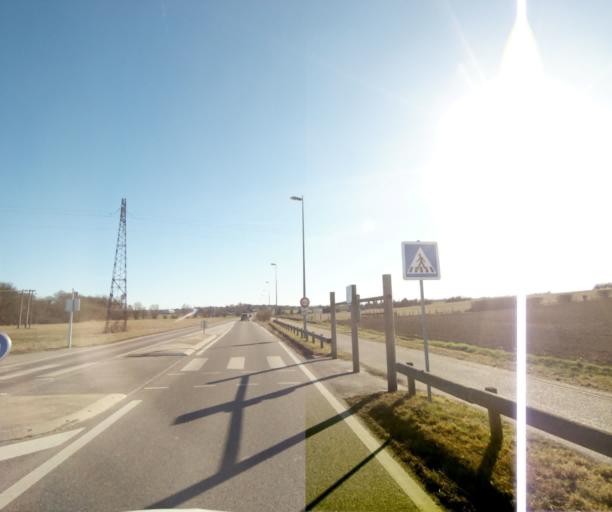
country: FR
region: Lorraine
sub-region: Departement de Meurthe-et-Moselle
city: Fleville-devant-Nancy
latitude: 48.6376
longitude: 6.2113
